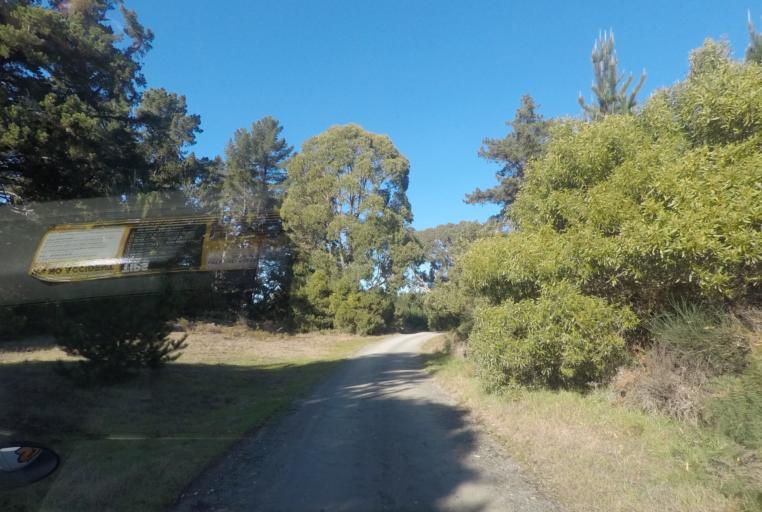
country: NZ
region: Tasman
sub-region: Tasman District
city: Mapua
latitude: -41.2638
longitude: 173.1426
